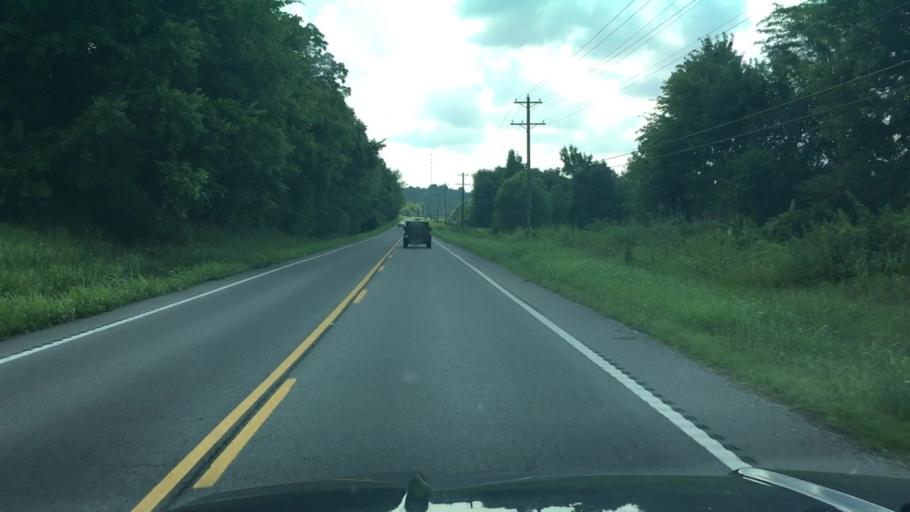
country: US
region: Tennessee
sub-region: Williamson County
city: Nolensville
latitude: 35.8586
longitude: -86.6775
